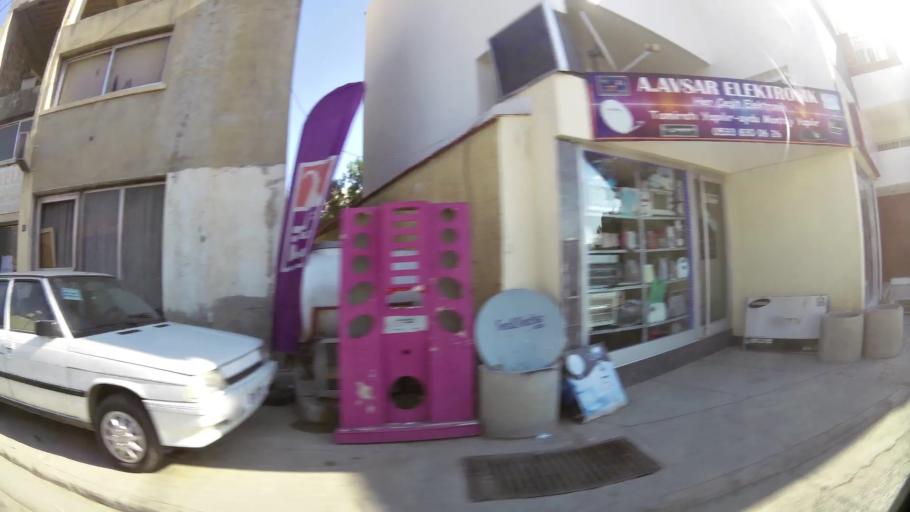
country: CY
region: Lefkosia
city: Nicosia
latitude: 35.2172
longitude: 33.3053
